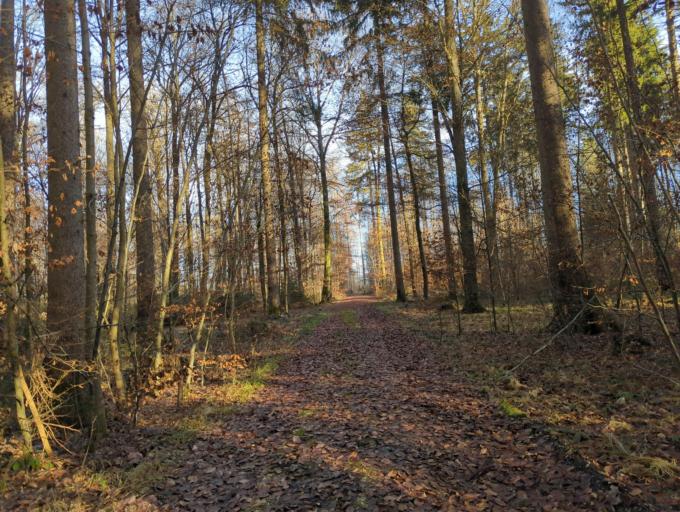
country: DE
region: Bavaria
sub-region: Swabia
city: Krumbach
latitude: 48.2497
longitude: 10.3939
